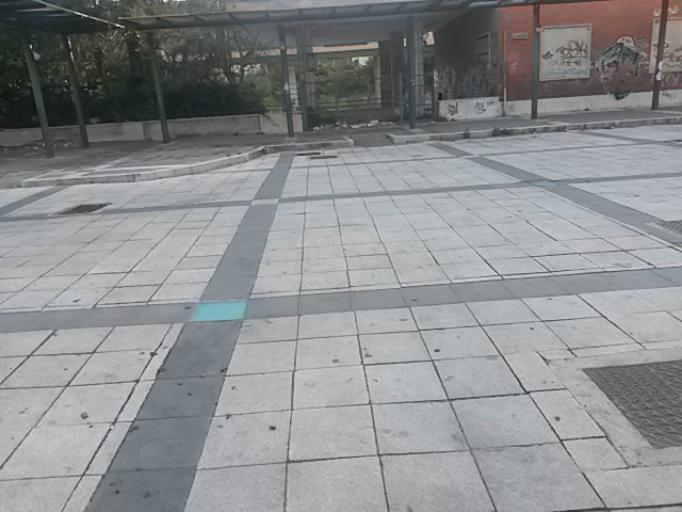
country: IT
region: Calabria
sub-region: Provincia di Catanzaro
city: Catanzaro
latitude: 38.8962
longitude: 16.5997
